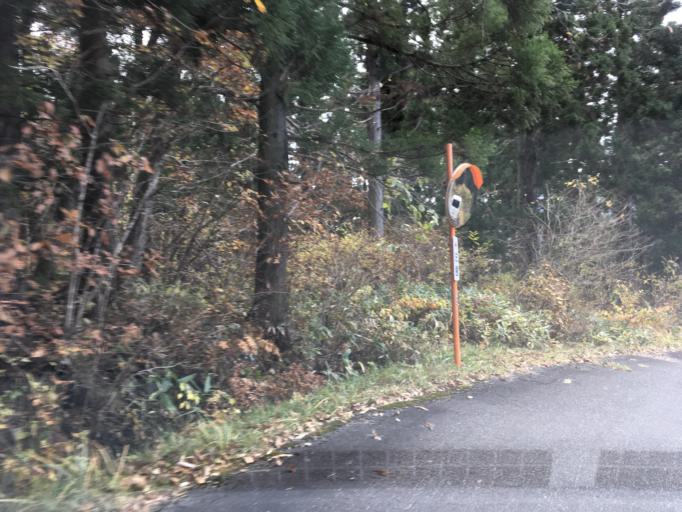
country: JP
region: Iwate
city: Mizusawa
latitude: 39.1248
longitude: 141.3221
